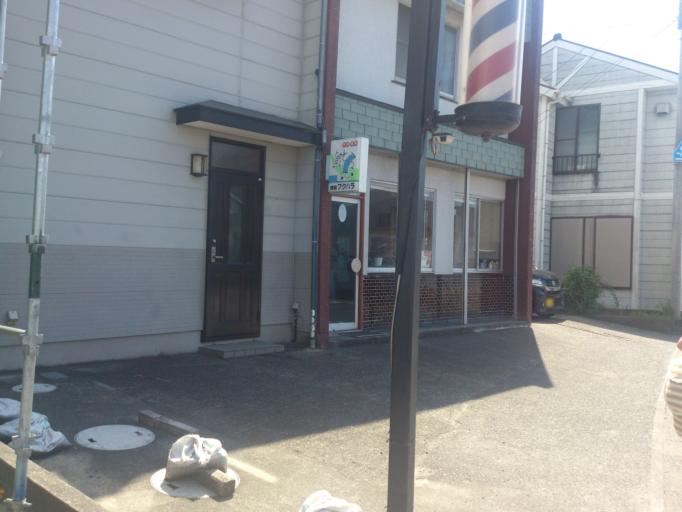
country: JP
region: Chiba
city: Tateyama
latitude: 35.1147
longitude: 139.8325
